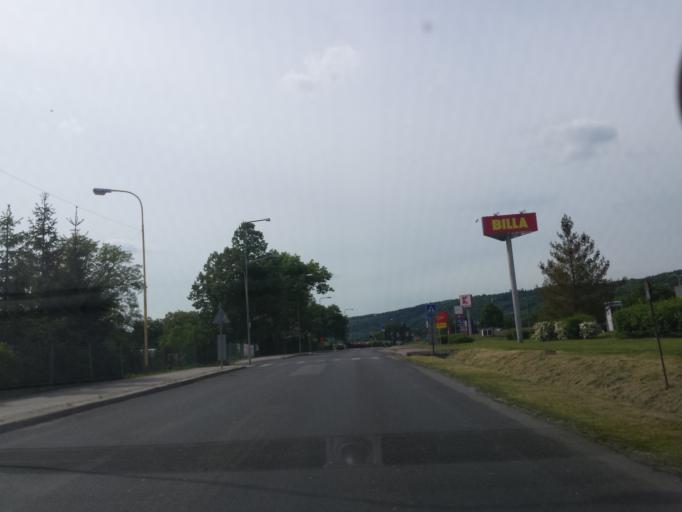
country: CZ
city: Novy Bor
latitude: 50.7638
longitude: 14.5471
